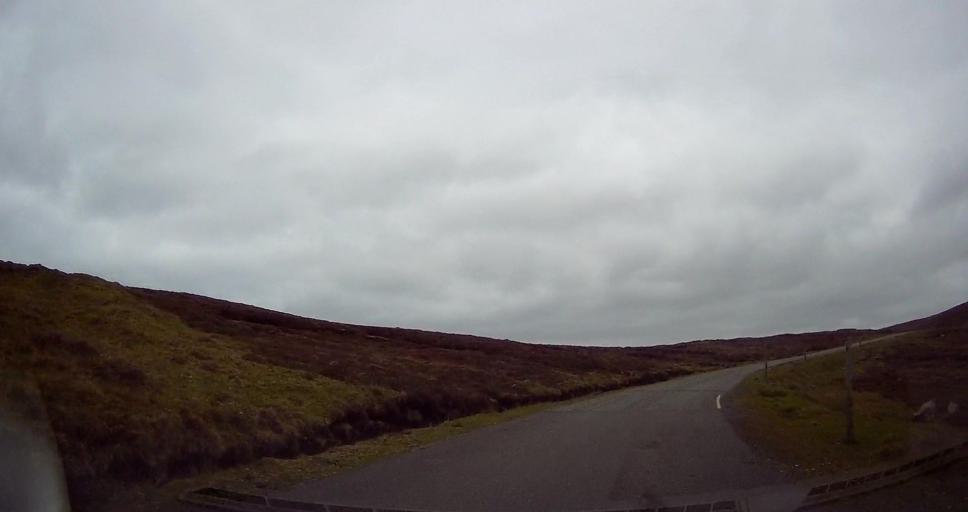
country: GB
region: Scotland
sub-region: Shetland Islands
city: Lerwick
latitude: 60.3188
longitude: -1.3421
